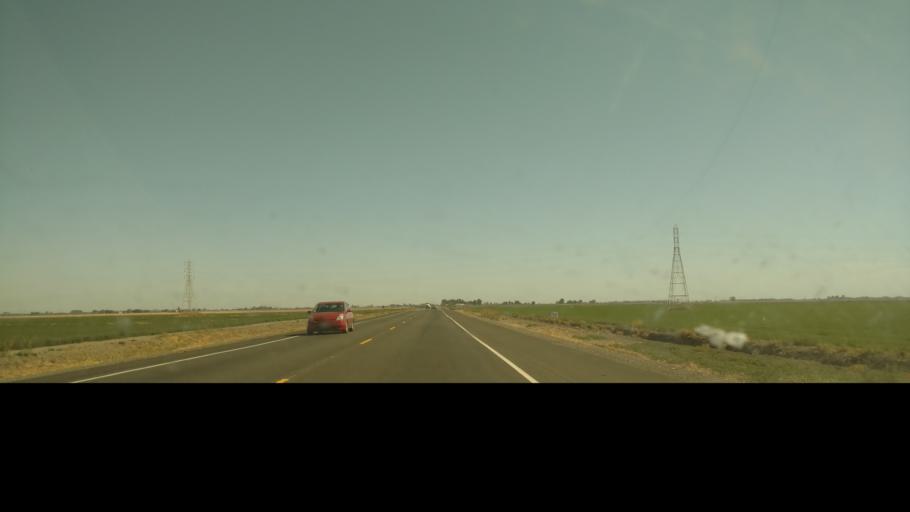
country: US
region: California
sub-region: Solano County
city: Rio Vista
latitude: 38.1483
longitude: -121.6540
